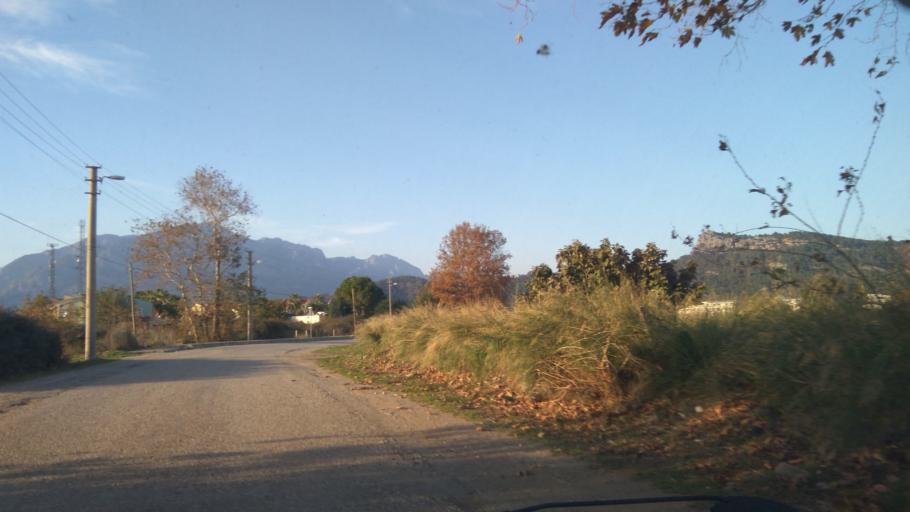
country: TR
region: Antalya
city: Kemer
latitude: 36.5615
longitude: 30.5720
